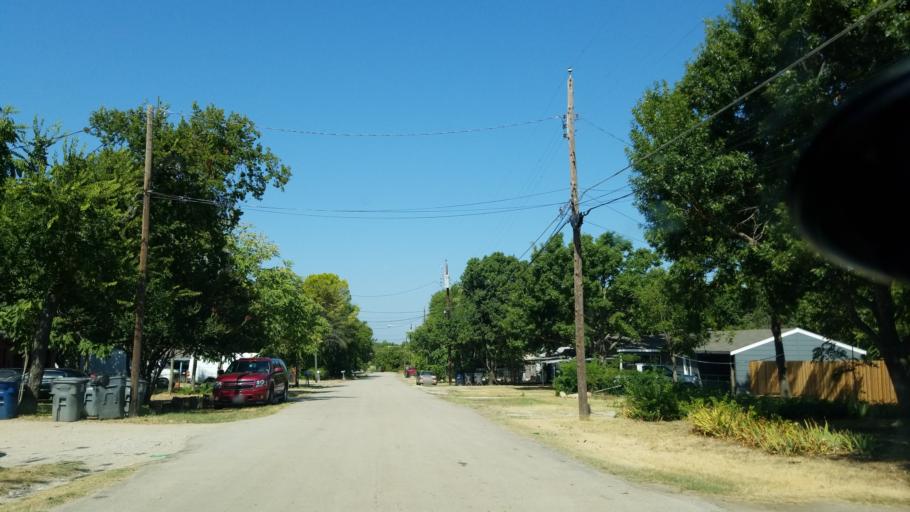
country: US
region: Texas
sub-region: Dallas County
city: Cockrell Hill
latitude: 32.7000
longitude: -96.9206
